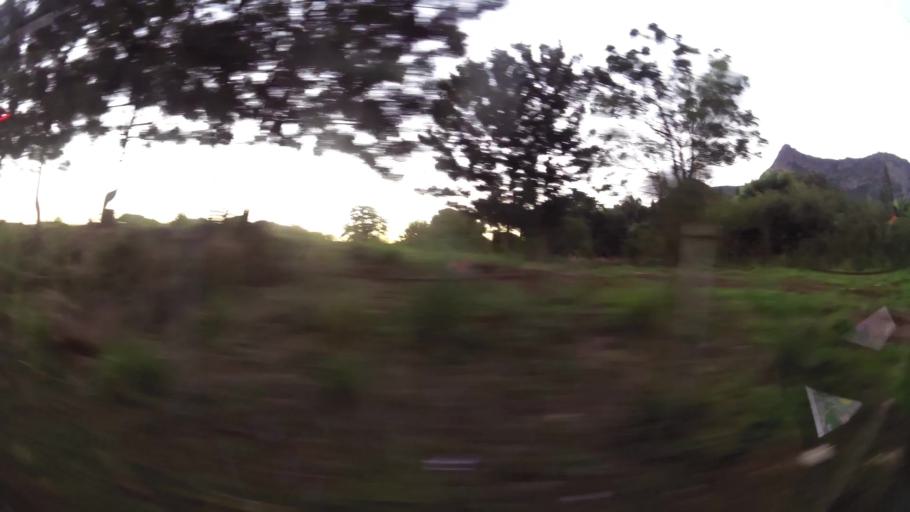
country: MU
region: Moka
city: Moka
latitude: -20.2242
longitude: 57.5003
